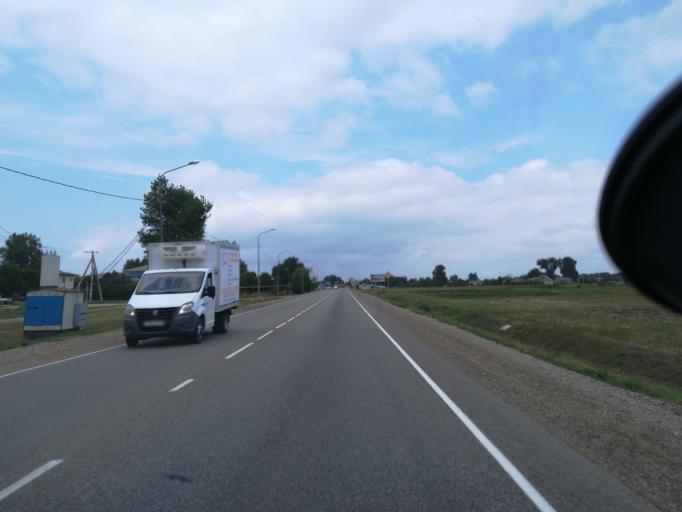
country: RU
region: Krasnodarskiy
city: Korzhevskiy
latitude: 45.1967
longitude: 37.6689
